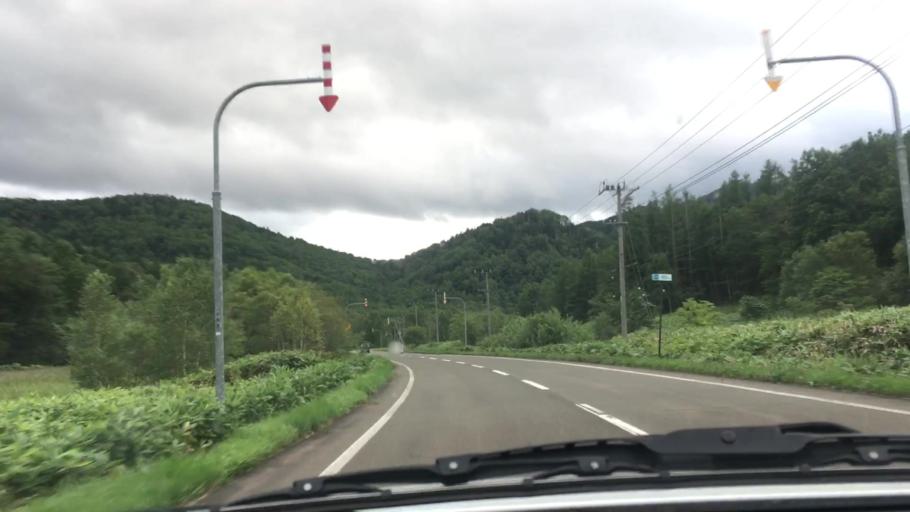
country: JP
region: Hokkaido
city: Shimo-furano
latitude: 43.0490
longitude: 142.5328
